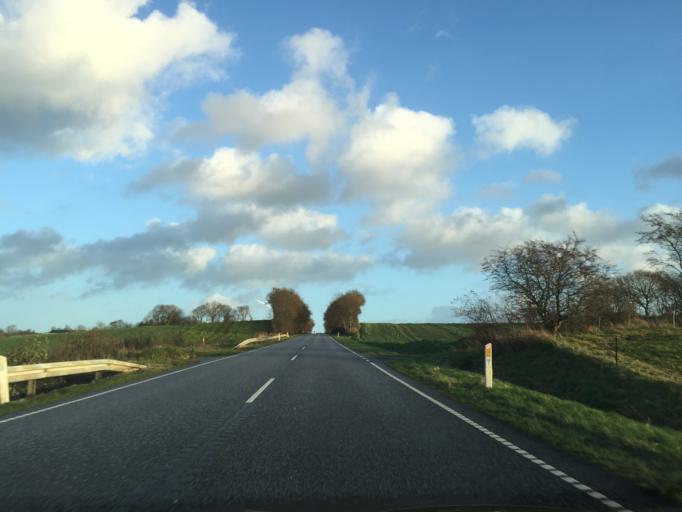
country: DK
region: Central Jutland
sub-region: Silkeborg Kommune
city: Kjellerup
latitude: 56.3034
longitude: 9.4799
